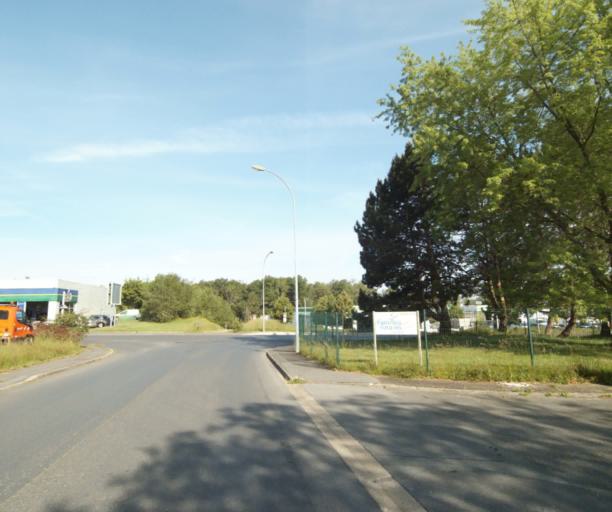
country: FR
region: Champagne-Ardenne
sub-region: Departement des Ardennes
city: La Francheville
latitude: 49.7394
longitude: 4.7018
